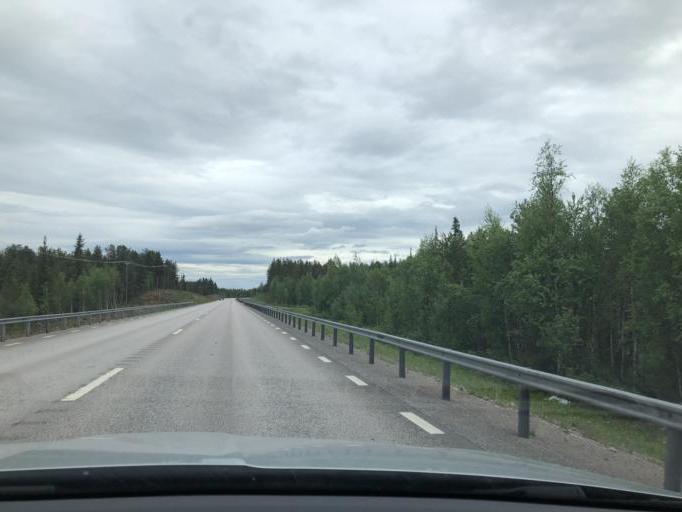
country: SE
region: Norrbotten
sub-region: Gallivare Kommun
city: Malmberget
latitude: 67.6420
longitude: 21.1003
